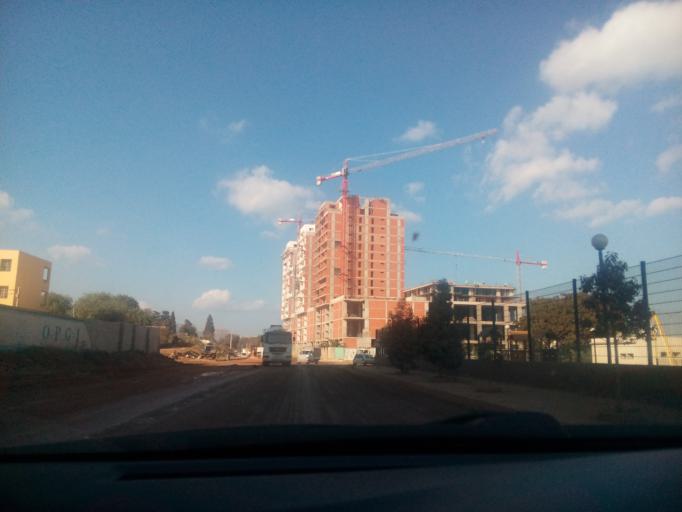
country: DZ
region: Oran
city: Es Senia
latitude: 35.6788
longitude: -0.6045
